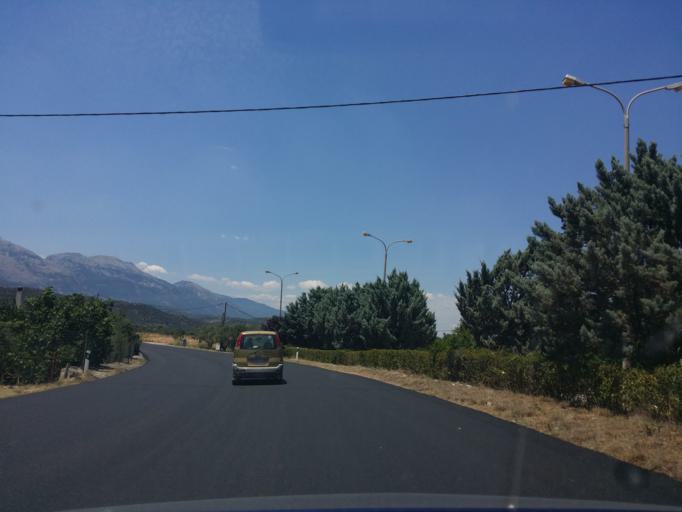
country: GR
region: Peloponnese
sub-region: Nomos Lakonias
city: Sparti
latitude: 37.0877
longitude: 22.4428
